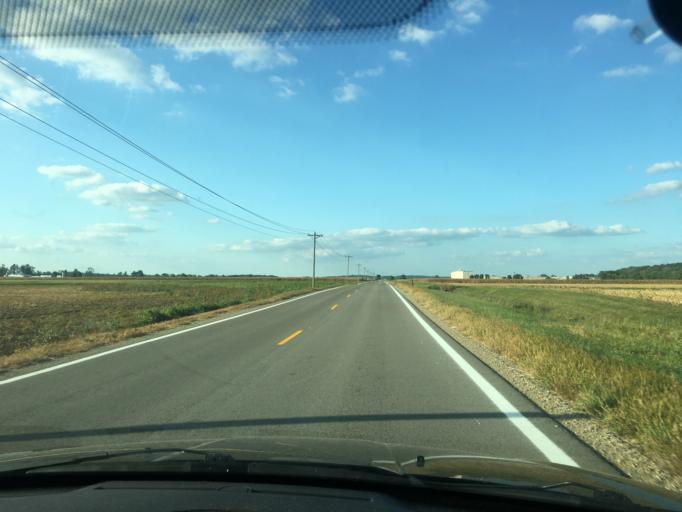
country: US
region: Ohio
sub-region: Champaign County
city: Urbana
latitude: 40.1762
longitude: -83.7828
